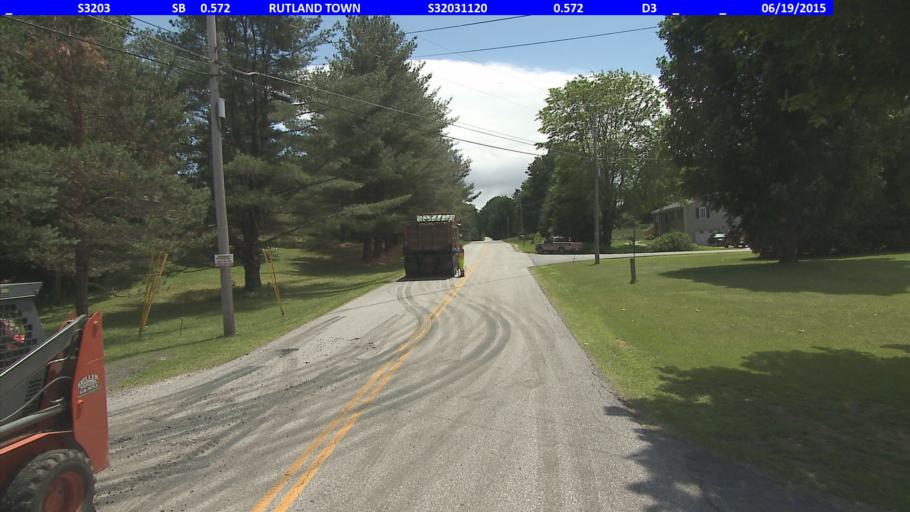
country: US
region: Vermont
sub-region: Rutland County
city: Rutland
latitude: 43.6614
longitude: -72.9991
